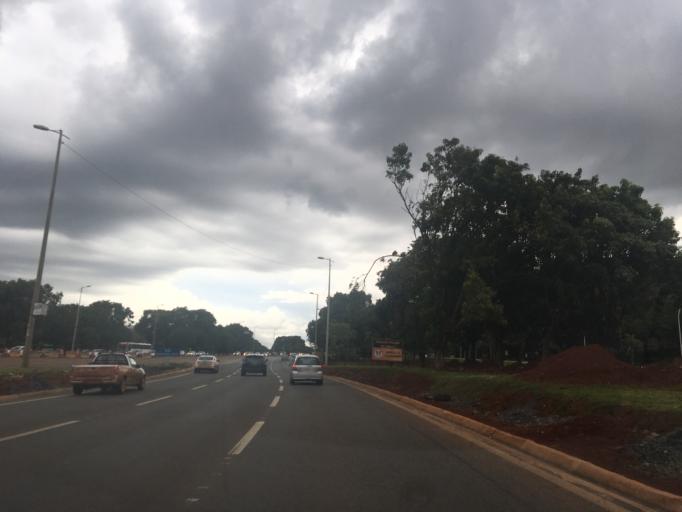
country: BR
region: Federal District
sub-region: Brasilia
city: Brasilia
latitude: -15.7359
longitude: -47.8929
